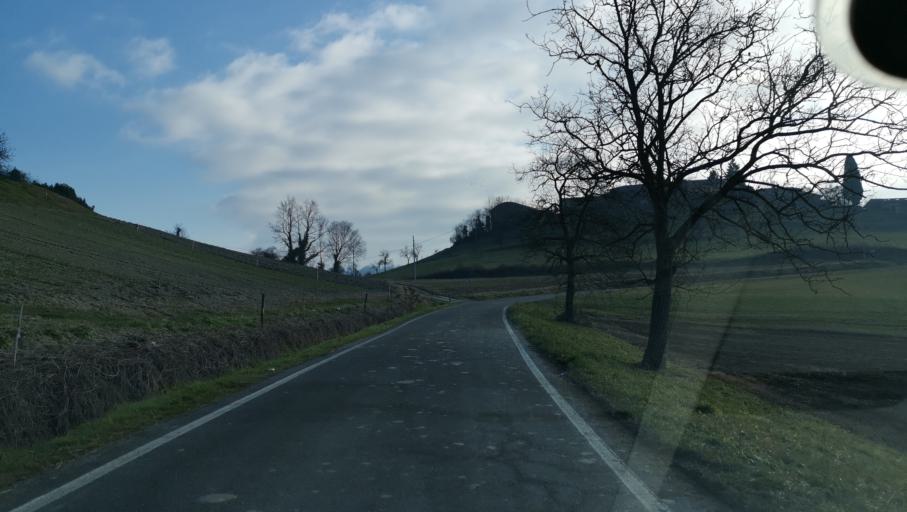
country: IT
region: Piedmont
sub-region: Provincia di Torino
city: Rivalba
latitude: 45.1055
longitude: 7.8904
